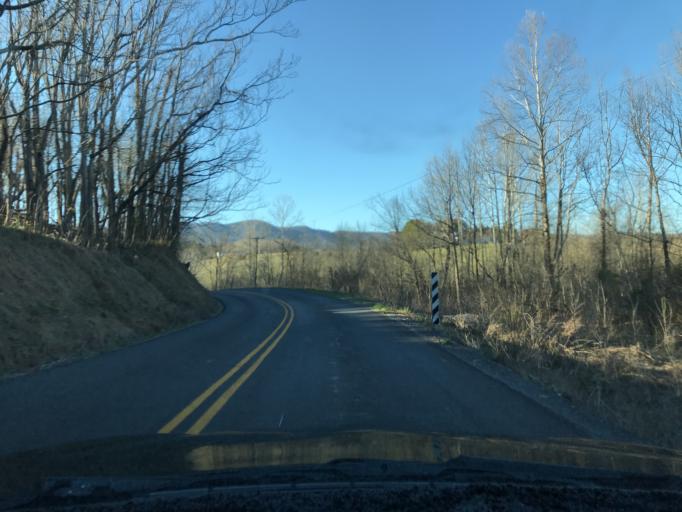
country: US
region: Virginia
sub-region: Botetourt County
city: Blue Ridge
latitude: 37.4045
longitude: -79.7030
